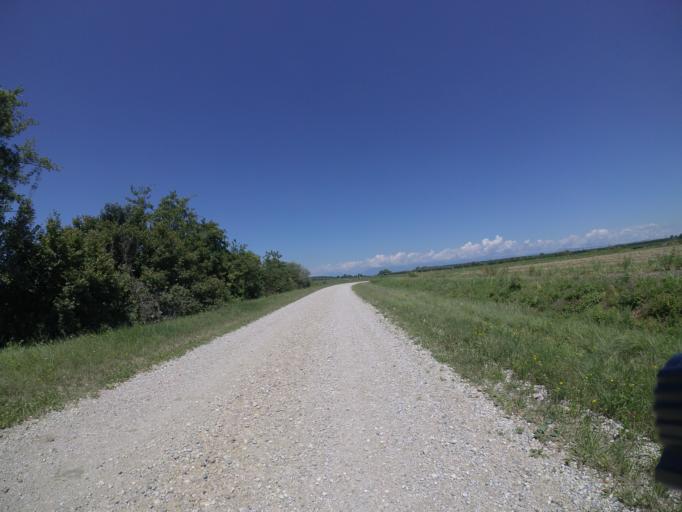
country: IT
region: Friuli Venezia Giulia
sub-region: Provincia di Udine
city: Talmassons
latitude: 45.8898
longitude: 13.0911
